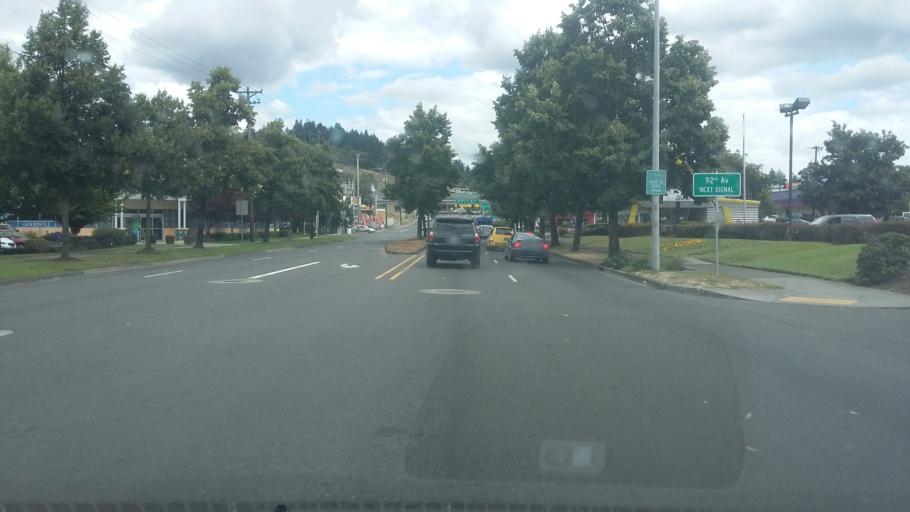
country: US
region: Oregon
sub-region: Multnomah County
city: Lents
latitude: 45.4974
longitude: -122.5709
